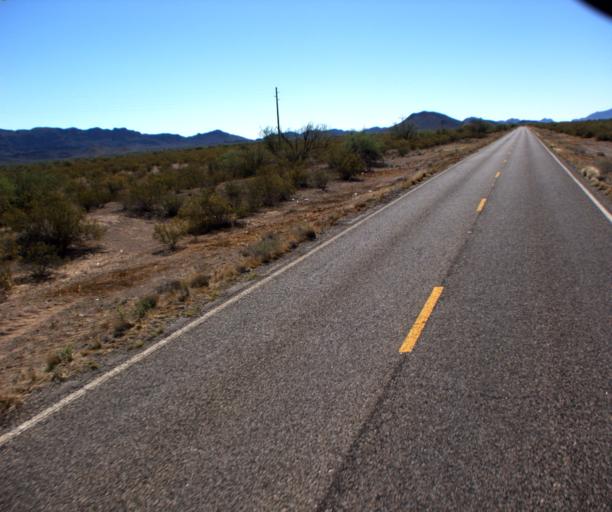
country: US
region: Arizona
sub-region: Pima County
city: Ajo
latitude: 32.3153
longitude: -112.7665
